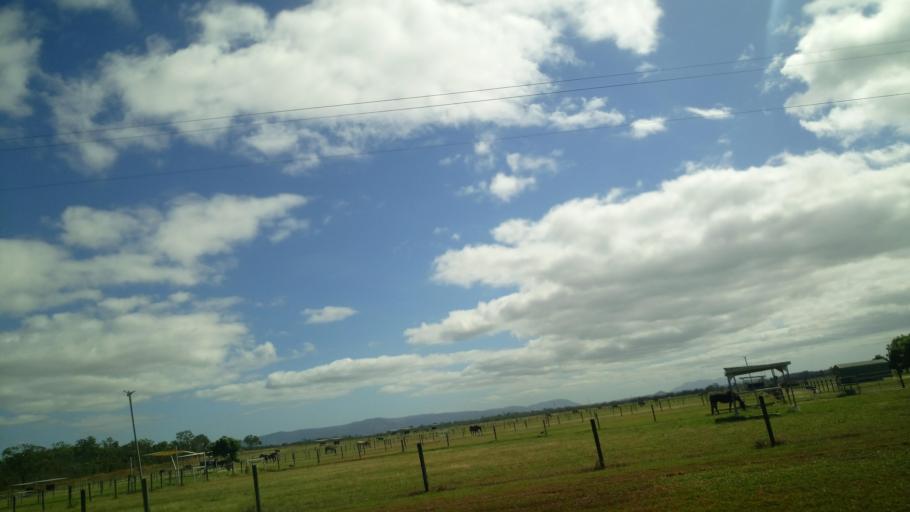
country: AU
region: Queensland
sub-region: Tablelands
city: Mareeba
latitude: -16.9732
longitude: 145.4581
